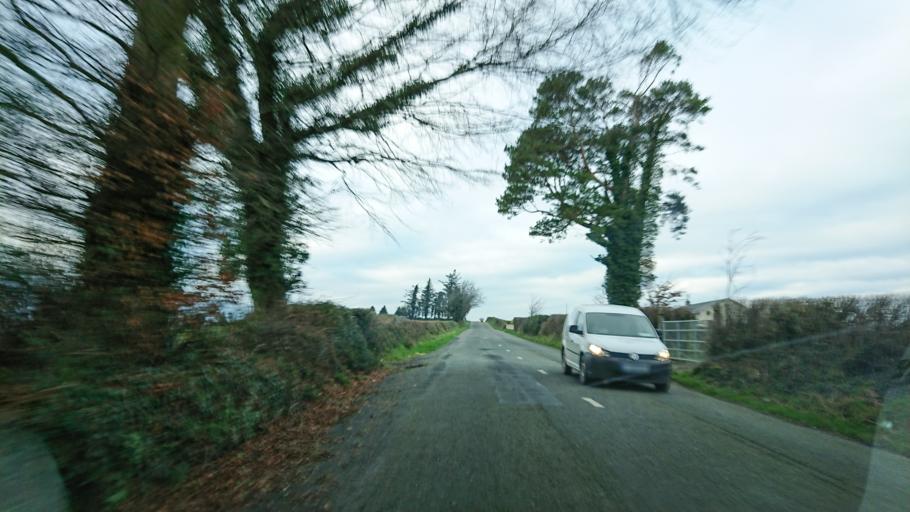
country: IE
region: Munster
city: Carrick-on-Suir
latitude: 52.3022
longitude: -7.4853
